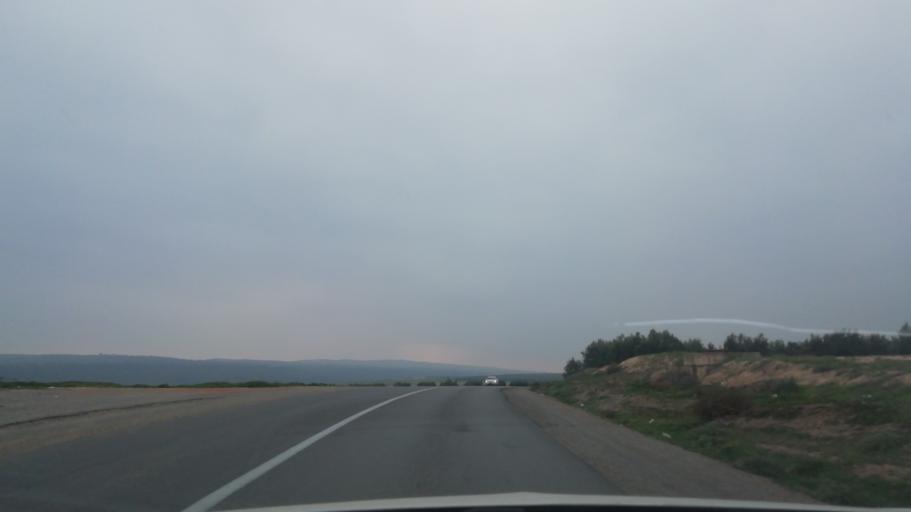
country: DZ
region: Sidi Bel Abbes
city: Sfizef
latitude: 35.2795
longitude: -0.1514
